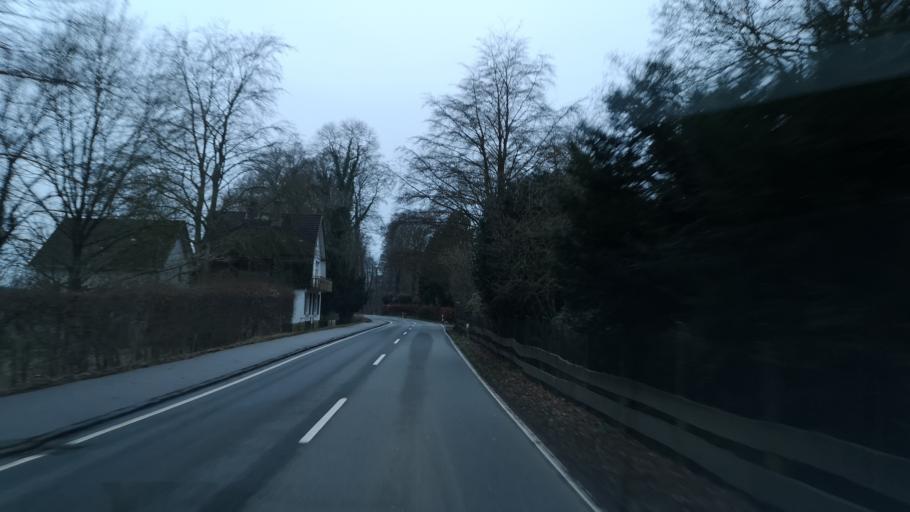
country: DE
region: Schleswig-Holstein
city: Munsterdorf
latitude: 53.9136
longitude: 9.5470
